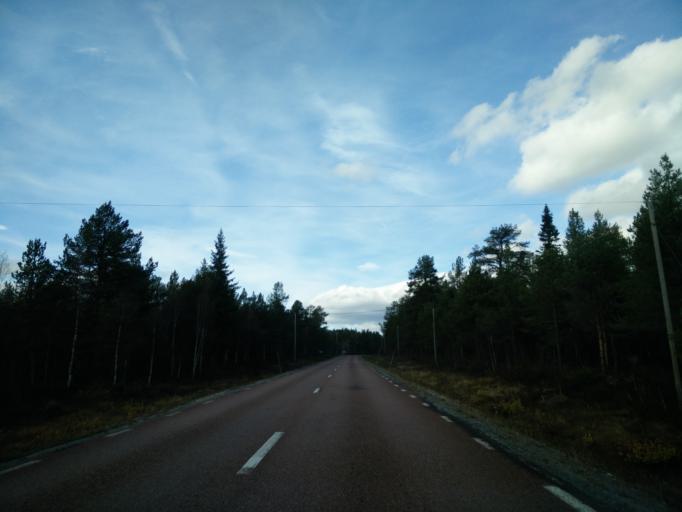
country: NO
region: Hedmark
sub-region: Engerdal
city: Engerdal
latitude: 62.4915
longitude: 12.6411
